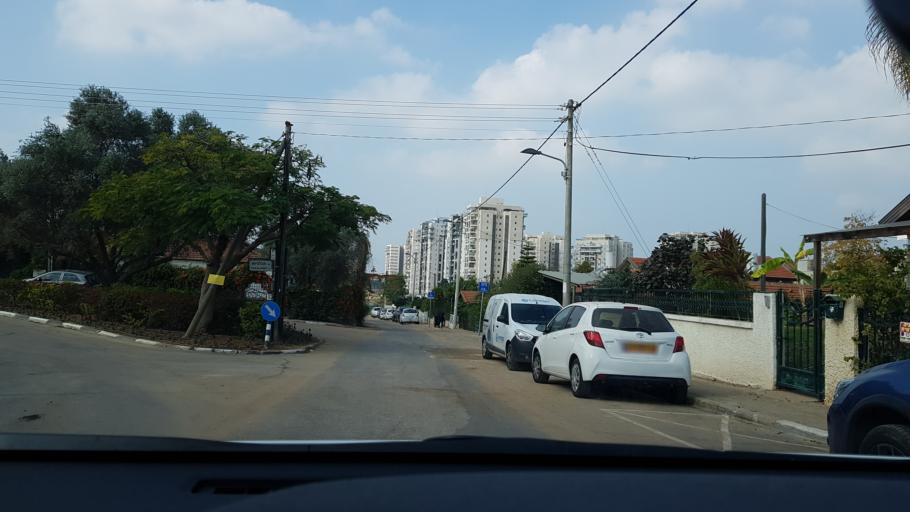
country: IL
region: Central District
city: Mazkeret Batya
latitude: 31.8774
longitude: 34.8134
